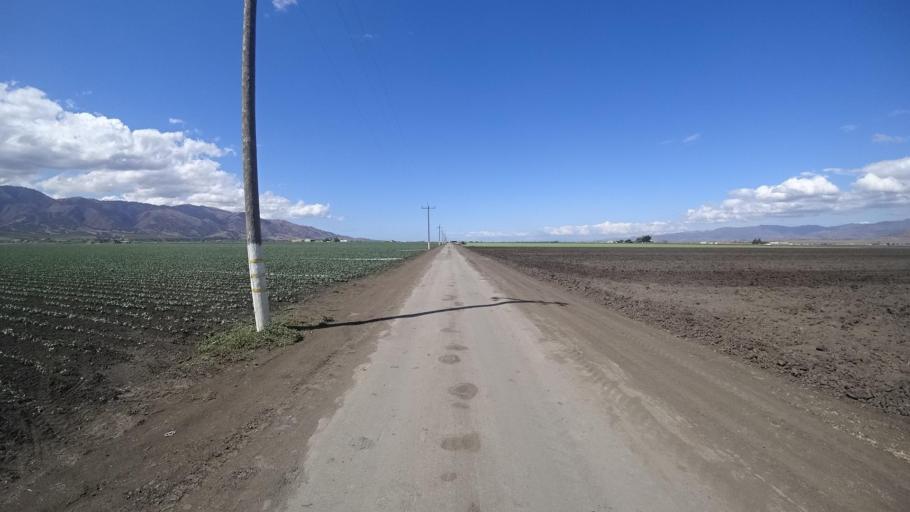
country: US
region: California
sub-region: Monterey County
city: Gonzales
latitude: 36.5109
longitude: -121.4774
